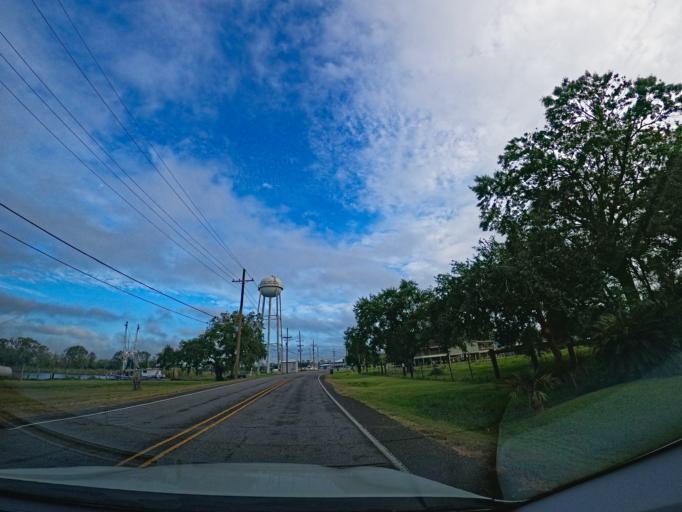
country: US
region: Louisiana
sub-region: Terrebonne Parish
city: Dulac
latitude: 29.3885
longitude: -90.7140
